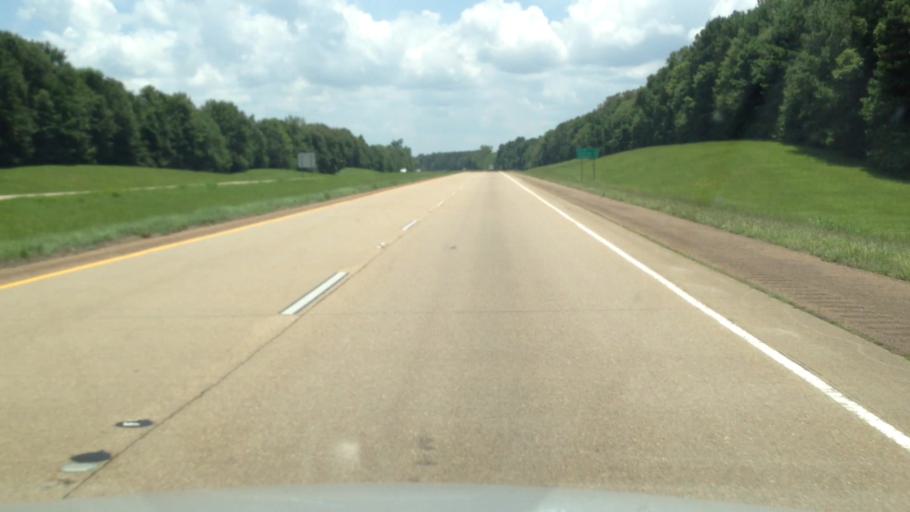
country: US
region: Louisiana
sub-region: Rapides Parish
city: Woodworth
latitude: 31.1510
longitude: -92.4536
